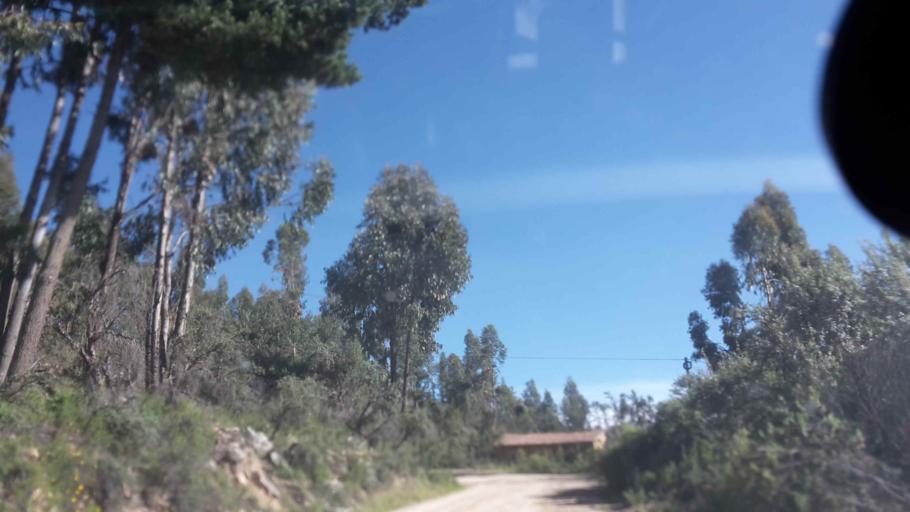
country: BO
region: Cochabamba
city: Arani
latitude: -17.6721
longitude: -65.7287
